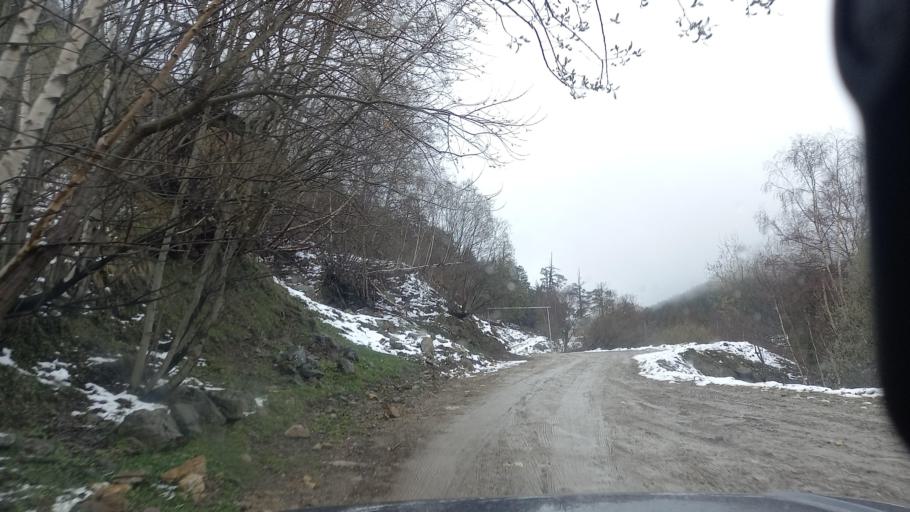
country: RU
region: Kabardino-Balkariya
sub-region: El'brusskiy Rayon
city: El'brus
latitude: 43.2238
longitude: 42.6800
